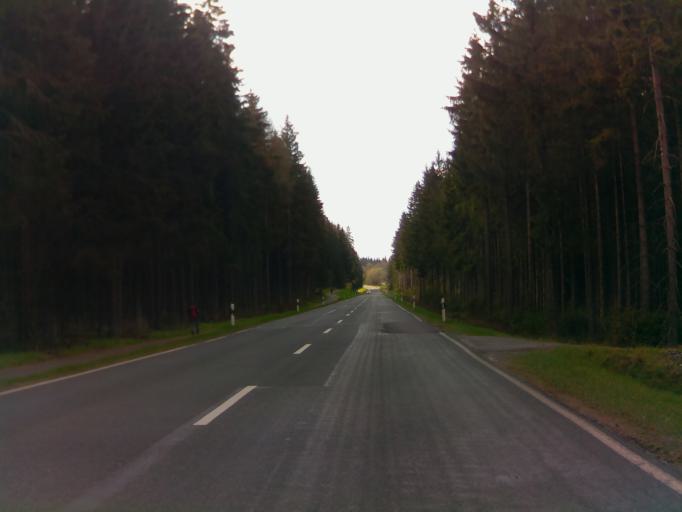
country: DE
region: Bavaria
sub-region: Upper Franconia
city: Ludwigsstadt
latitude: 50.4610
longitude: 11.3412
